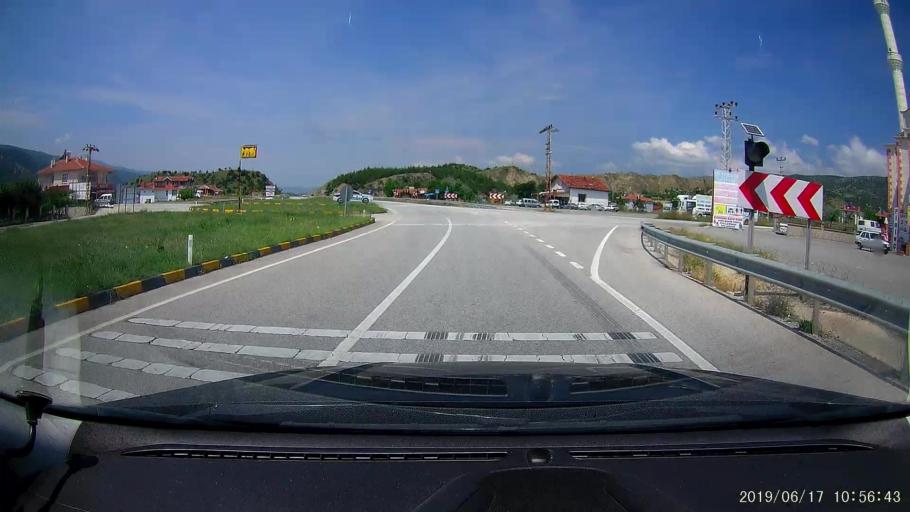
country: TR
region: Corum
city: Hacihamza
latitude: 41.0527
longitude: 34.2581
